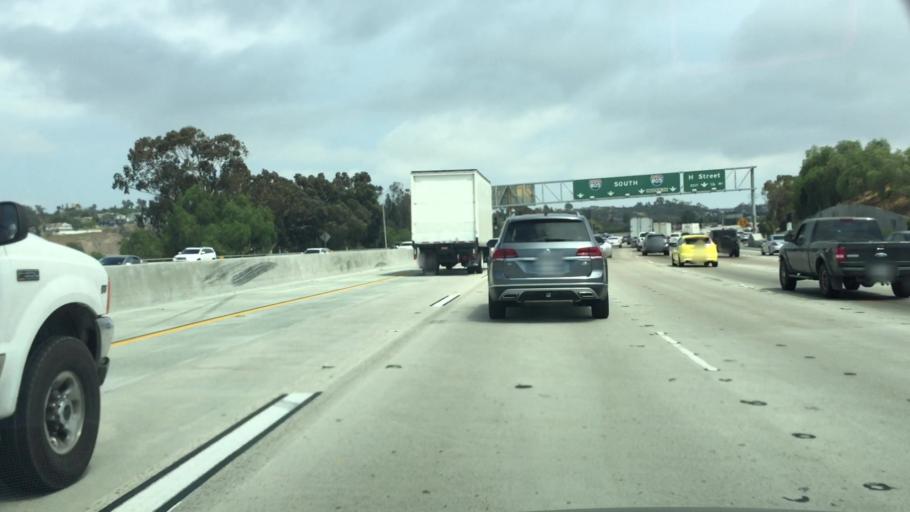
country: US
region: California
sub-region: San Diego County
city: Chula Vista
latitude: 32.6481
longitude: -117.0614
